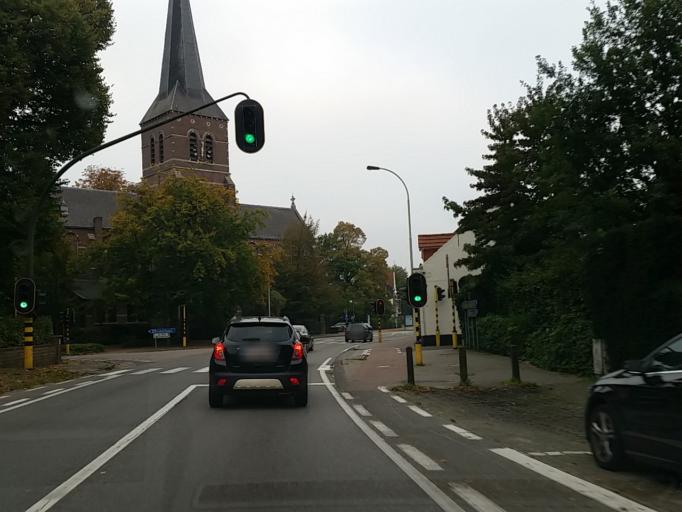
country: BE
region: Flanders
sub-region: Provincie Antwerpen
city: Kapellen
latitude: 51.2807
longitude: 4.4524
